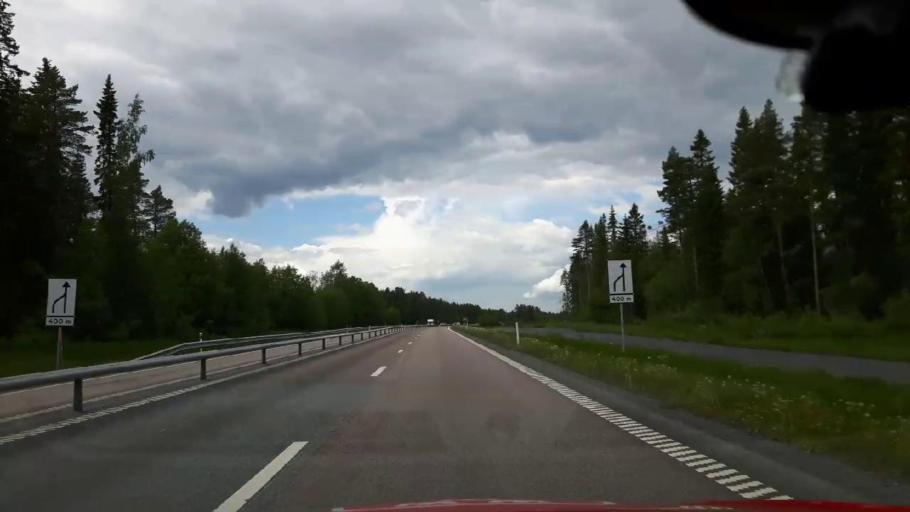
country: SE
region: Jaemtland
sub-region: OEstersunds Kommun
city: Ostersund
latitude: 63.2544
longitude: 14.5697
